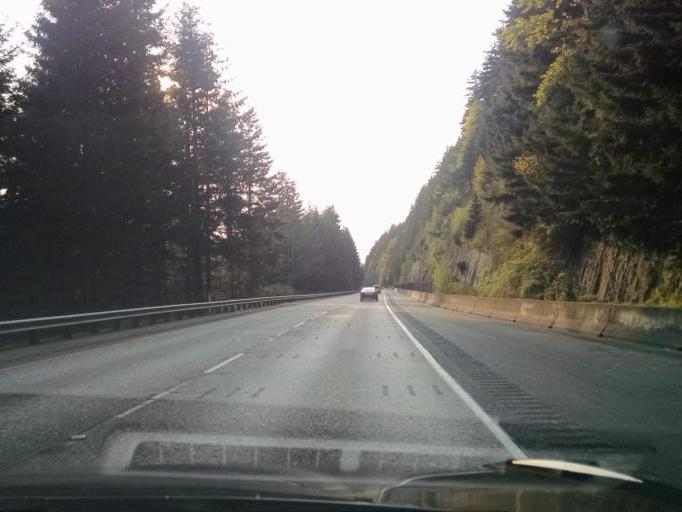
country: US
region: Washington
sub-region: Whatcom County
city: Geneva
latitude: 48.6912
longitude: -122.4330
